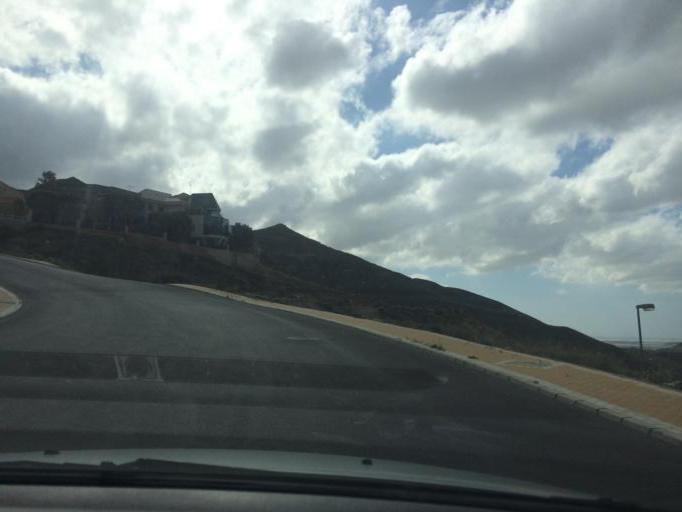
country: ES
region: Andalusia
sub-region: Provincia de Almeria
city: Vicar
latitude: 36.8347
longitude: -2.6131
